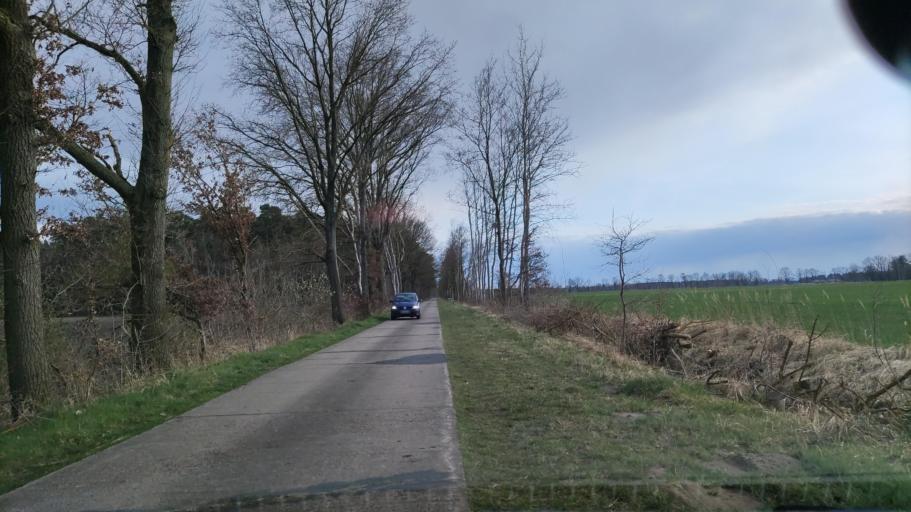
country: DE
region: Lower Saxony
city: Trebel
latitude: 53.0199
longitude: 11.2697
